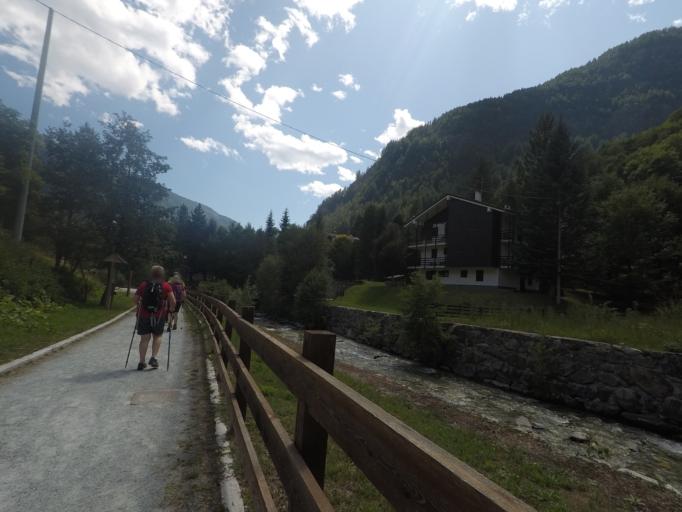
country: IT
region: Aosta Valley
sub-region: Valle d'Aosta
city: Paquier
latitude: 45.8838
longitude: 7.6224
